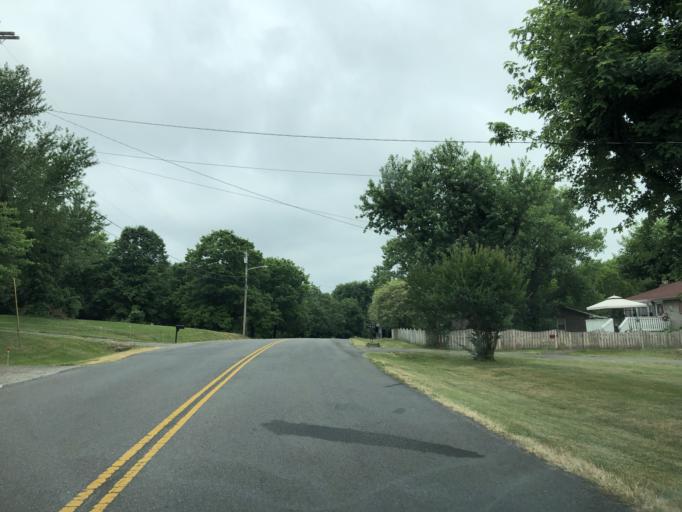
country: US
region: Tennessee
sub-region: Davidson County
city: Goodlettsville
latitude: 36.2833
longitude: -86.7282
